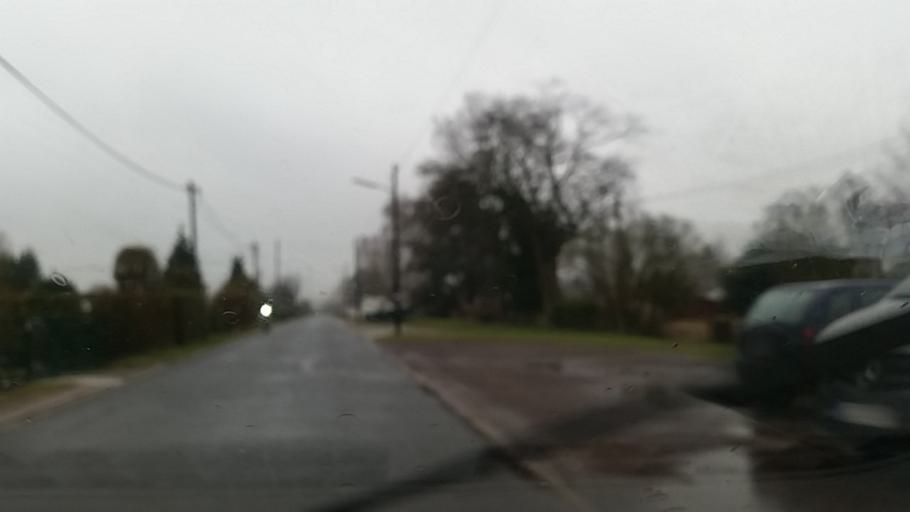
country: DE
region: Hamburg
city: Marienthal
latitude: 53.5428
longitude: 10.0684
